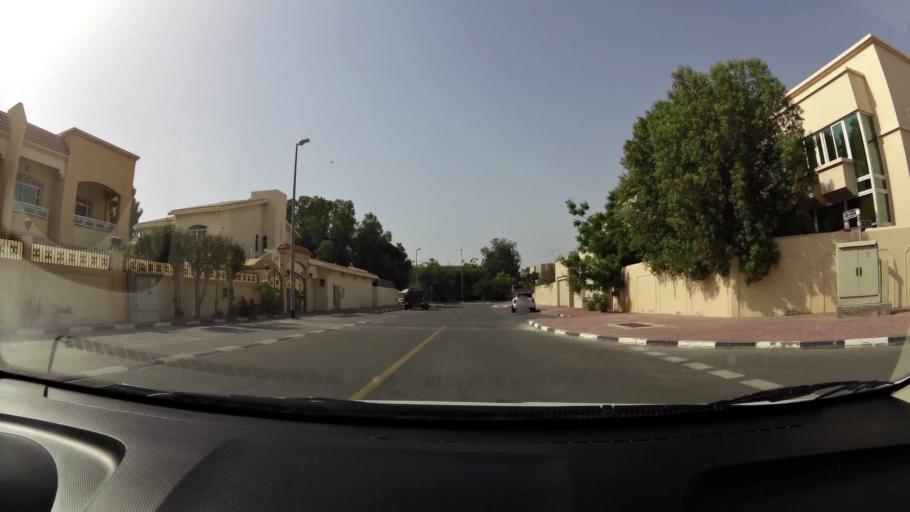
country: AE
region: Ash Shariqah
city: Sharjah
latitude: 25.2399
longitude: 55.3527
